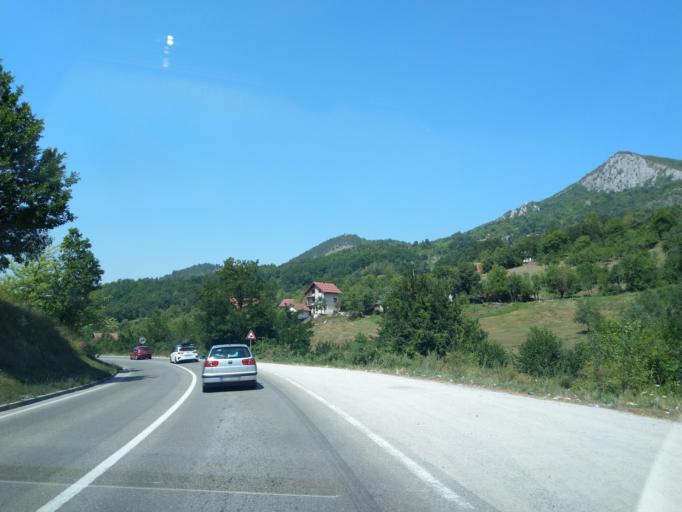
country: RS
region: Central Serbia
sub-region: Zlatiborski Okrug
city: Prijepolje
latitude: 43.4671
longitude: 19.6711
